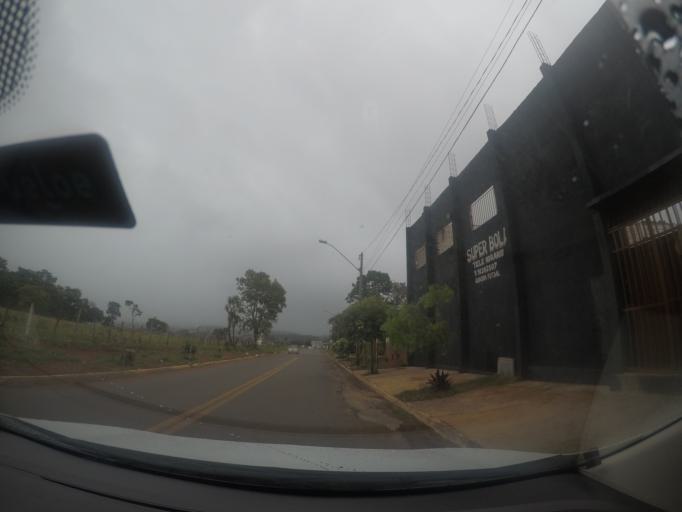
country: BR
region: Goias
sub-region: Goiania
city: Goiania
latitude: -16.6140
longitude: -49.3508
